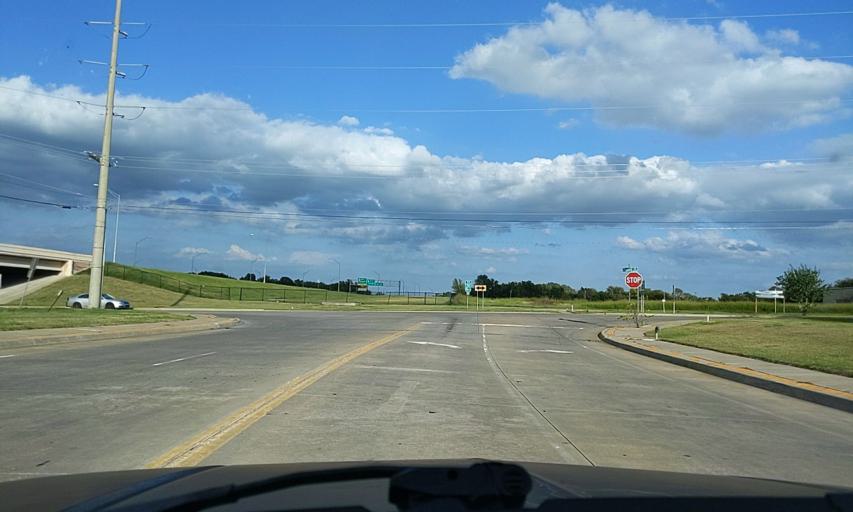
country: US
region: Oklahoma
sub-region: Tulsa County
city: Turley
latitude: 36.1965
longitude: -95.9762
